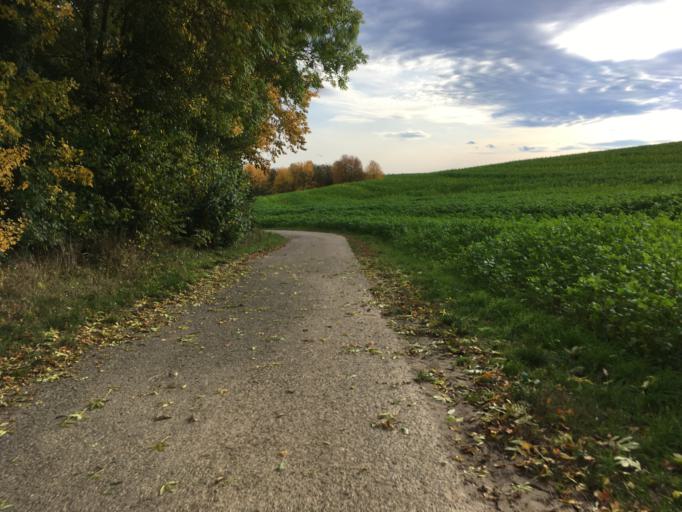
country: DE
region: Baden-Wuerttemberg
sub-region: Karlsruhe Region
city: Sinsheim
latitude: 49.2647
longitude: 8.8990
